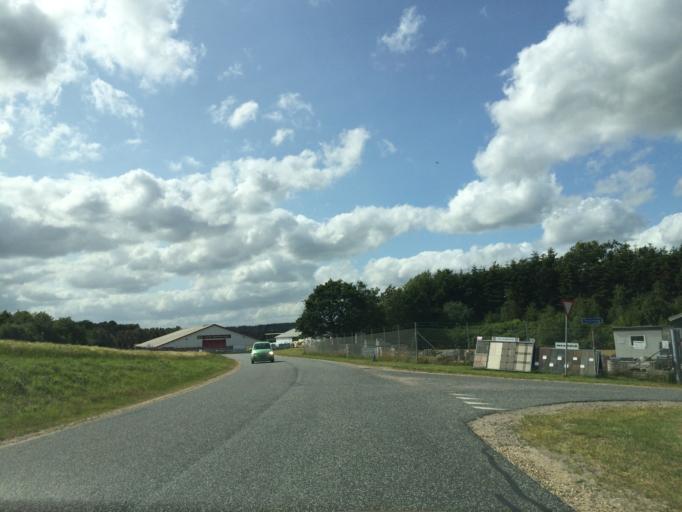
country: DK
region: Central Jutland
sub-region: Favrskov Kommune
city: Hammel
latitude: 56.2189
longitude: 9.7453
